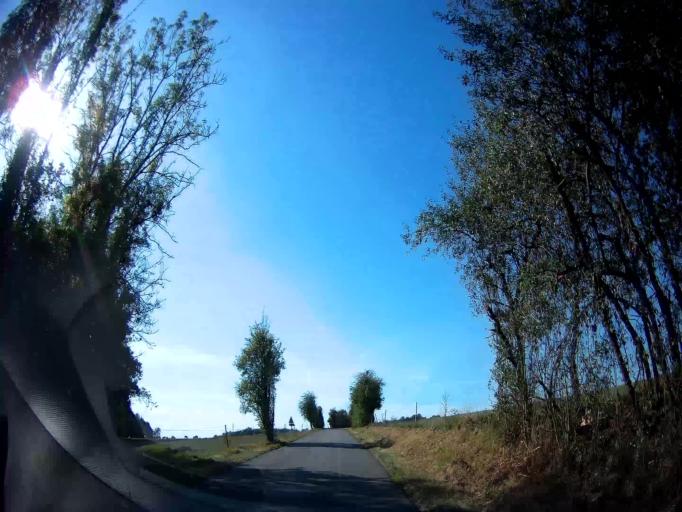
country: BE
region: Wallonia
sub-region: Province de Namur
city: Dinant
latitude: 50.2473
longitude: 4.9474
